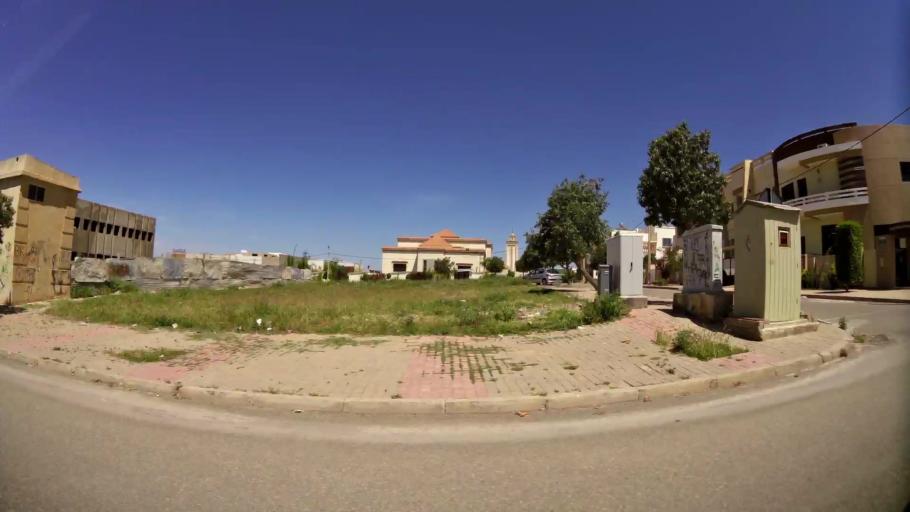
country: MA
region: Oriental
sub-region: Oujda-Angad
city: Oujda
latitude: 34.6541
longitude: -1.9155
